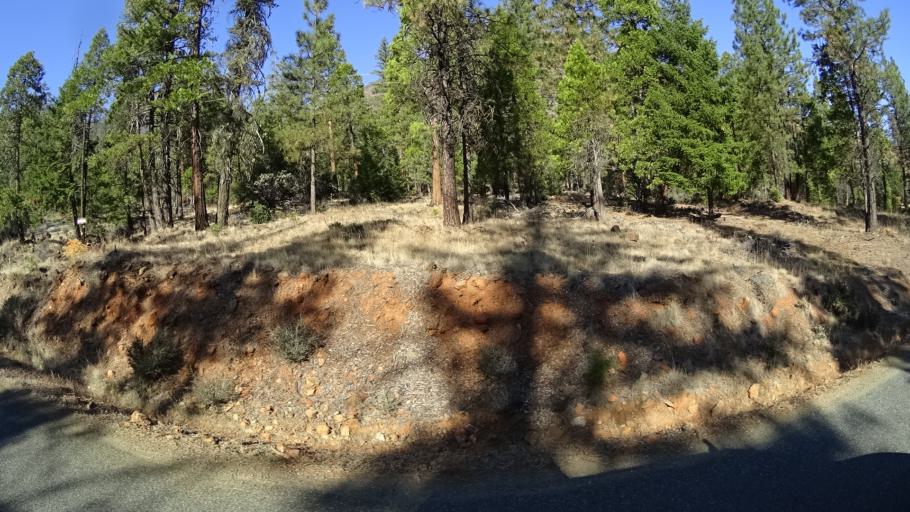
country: US
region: California
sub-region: Siskiyou County
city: Happy Camp
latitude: 41.7140
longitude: -123.0245
